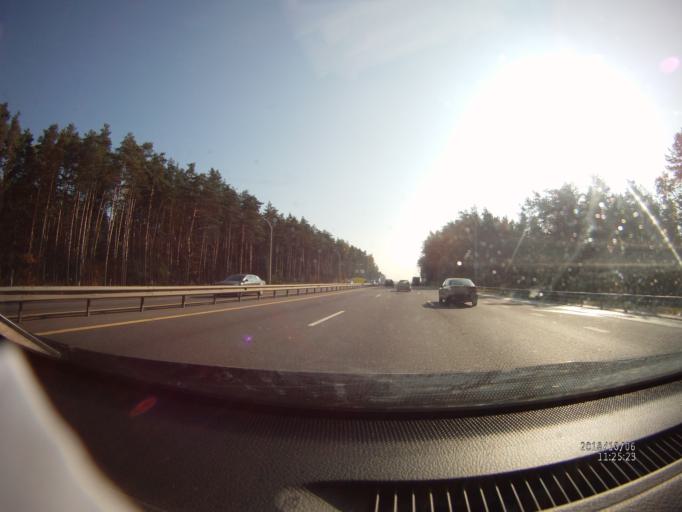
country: BY
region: Minsk
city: Bal'shavik
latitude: 53.9677
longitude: 27.6042
